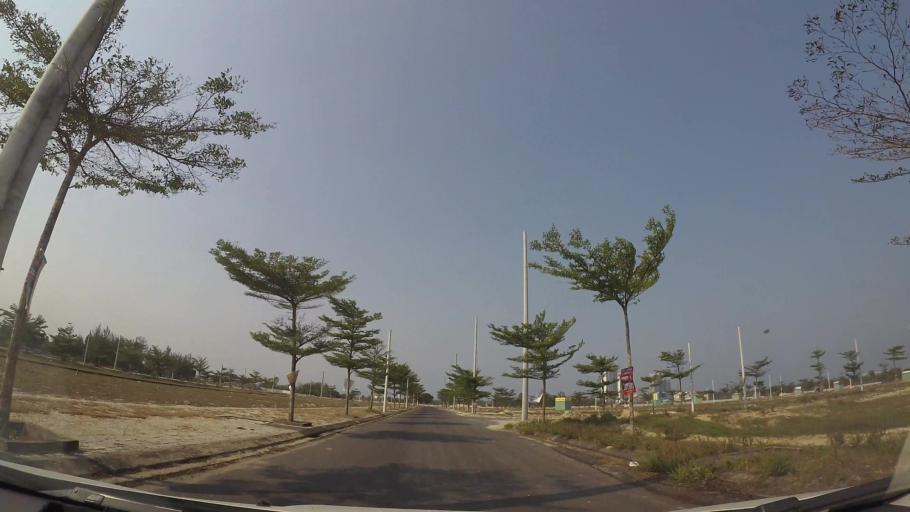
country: VN
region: Da Nang
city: Ngu Hanh Son
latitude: 15.9553
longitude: 108.2731
